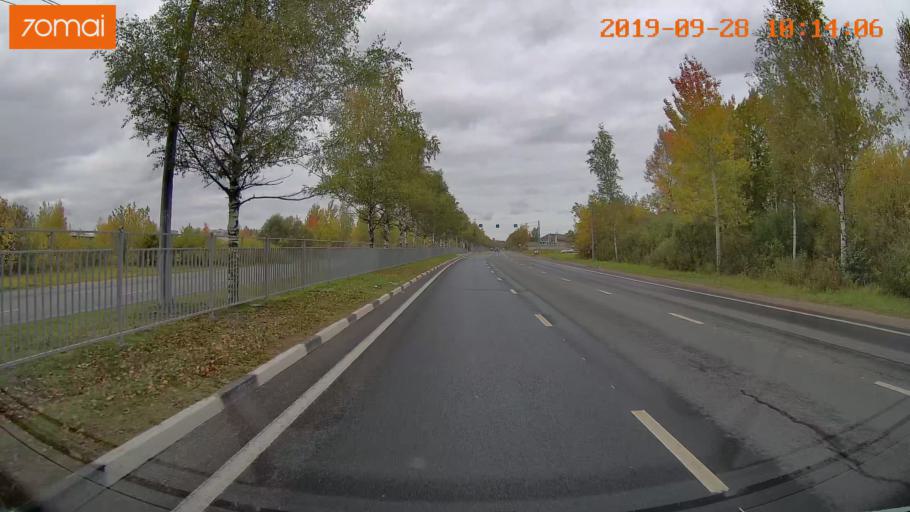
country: RU
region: Jaroslavl
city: Yaroslavl
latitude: 57.5489
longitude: 39.9565
